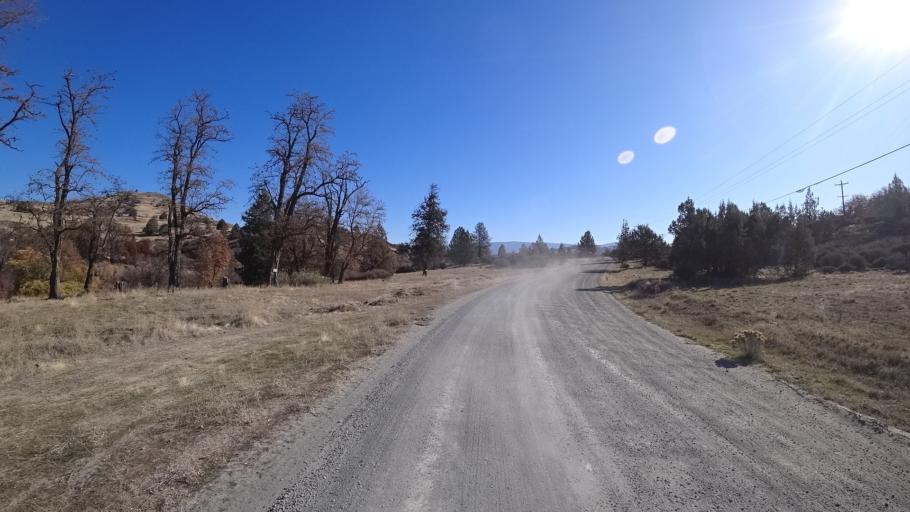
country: US
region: California
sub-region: Siskiyou County
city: Montague
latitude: 41.8989
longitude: -122.5113
